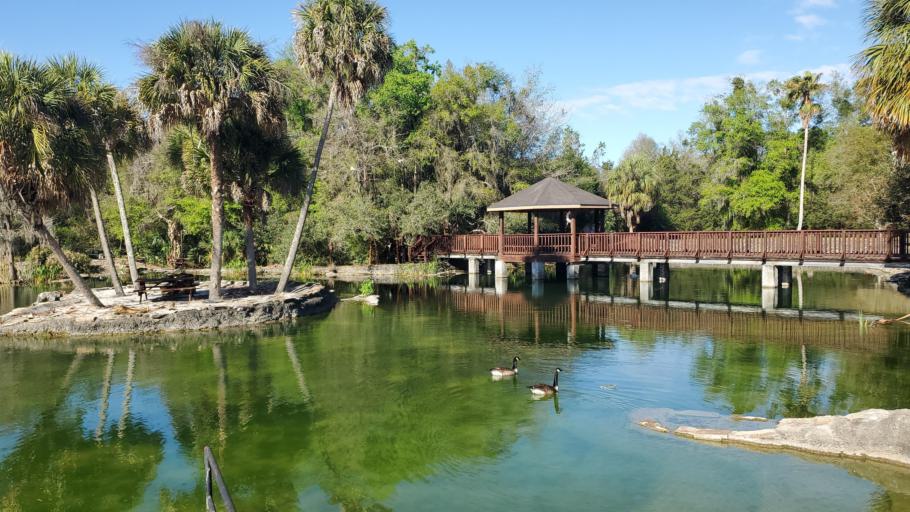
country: US
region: Florida
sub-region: Levy County
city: Williston
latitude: 29.4070
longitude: -82.4761
